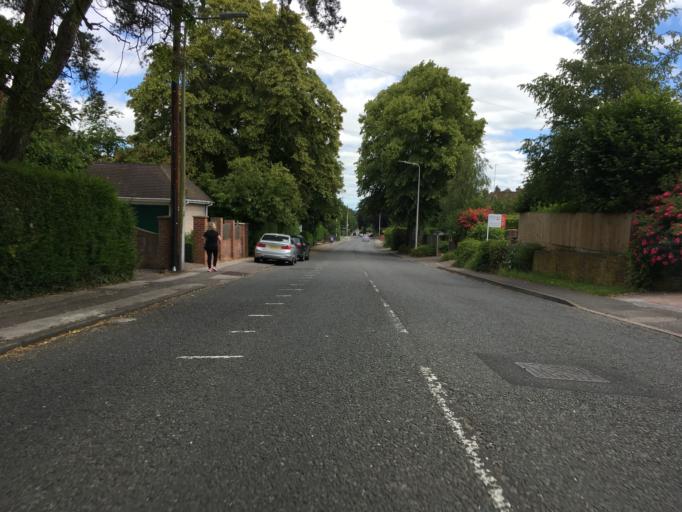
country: GB
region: England
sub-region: West Berkshire
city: Newbury
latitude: 51.3888
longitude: -1.3335
